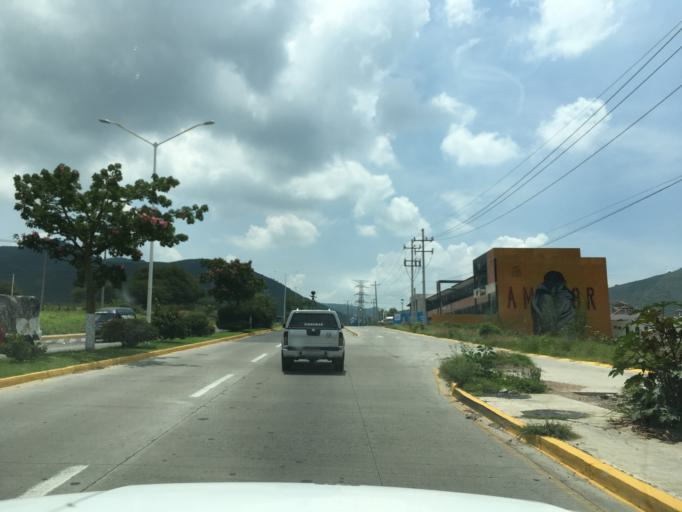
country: MX
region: Jalisco
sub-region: Tlajomulco de Zuniga
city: Santa Cruz de las Flores
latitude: 20.4904
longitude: -103.4856
